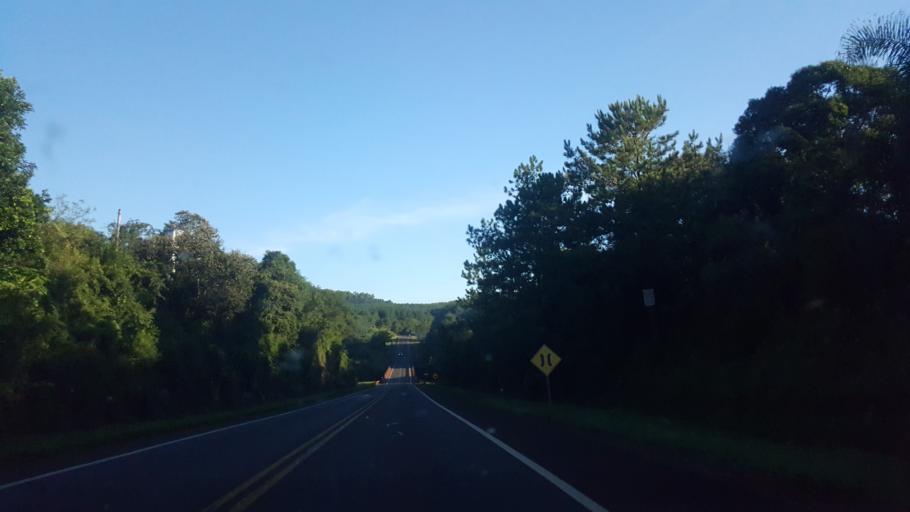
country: AR
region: Misiones
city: Caraguatay
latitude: -26.6557
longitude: -54.7538
